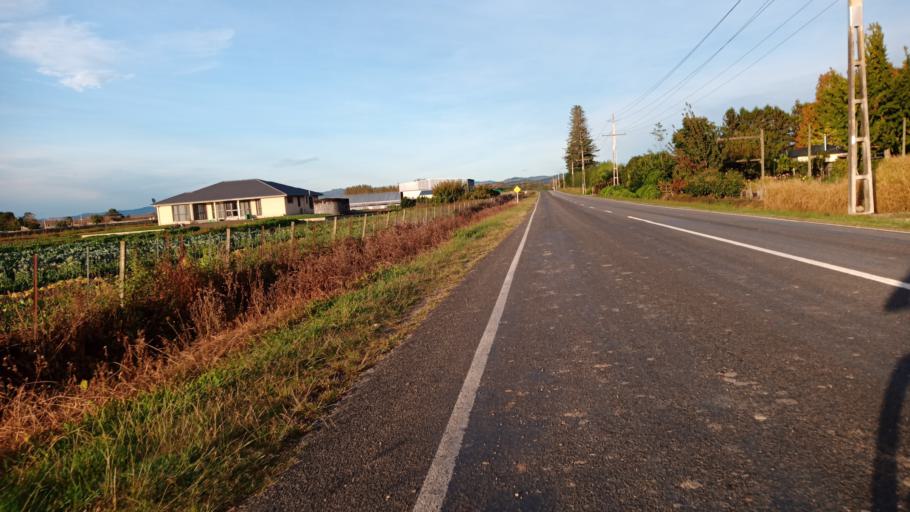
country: NZ
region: Gisborne
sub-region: Gisborne District
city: Gisborne
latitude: -38.6484
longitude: 177.9467
